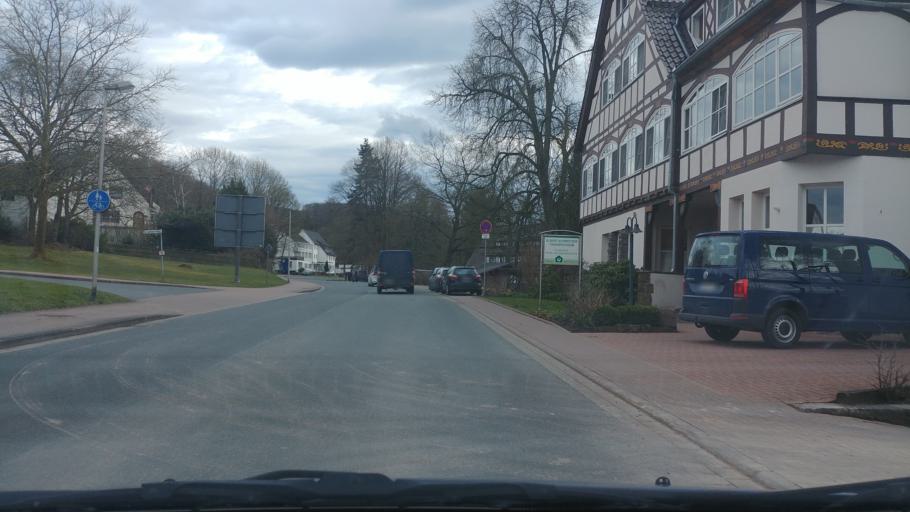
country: DE
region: Lower Saxony
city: Bevern
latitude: 51.8248
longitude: 9.4833
